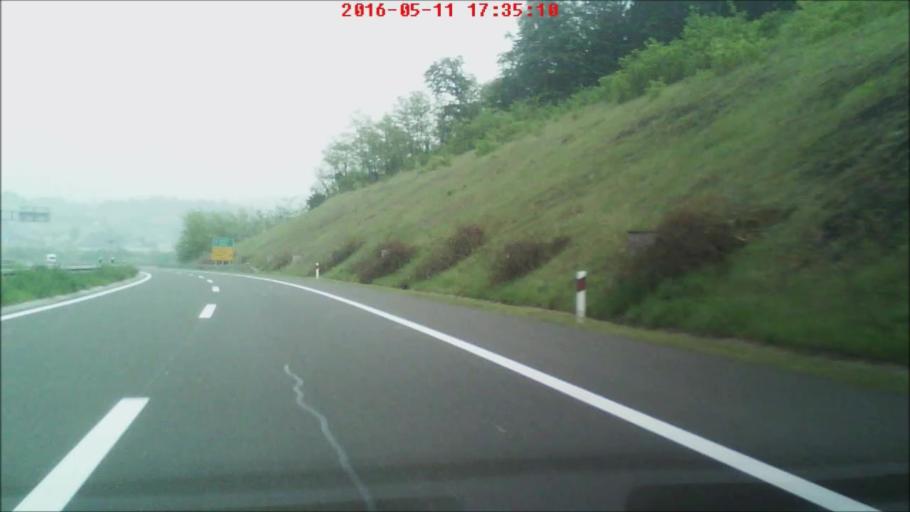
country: HR
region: Krapinsko-Zagorska
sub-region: Grad Krapina
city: Krapina
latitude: 46.1339
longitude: 15.8723
